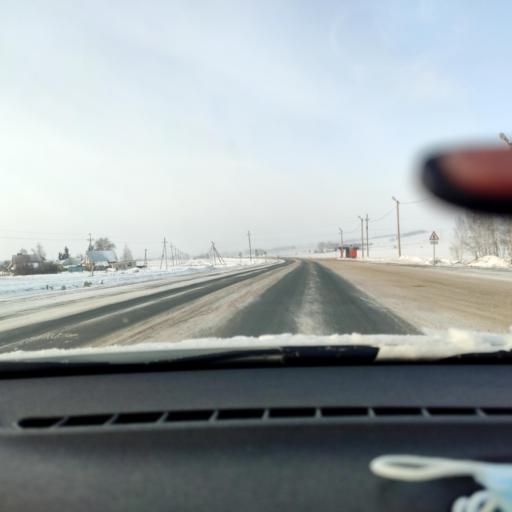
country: RU
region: Bashkortostan
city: Karmaskaly
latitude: 54.3888
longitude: 56.2393
